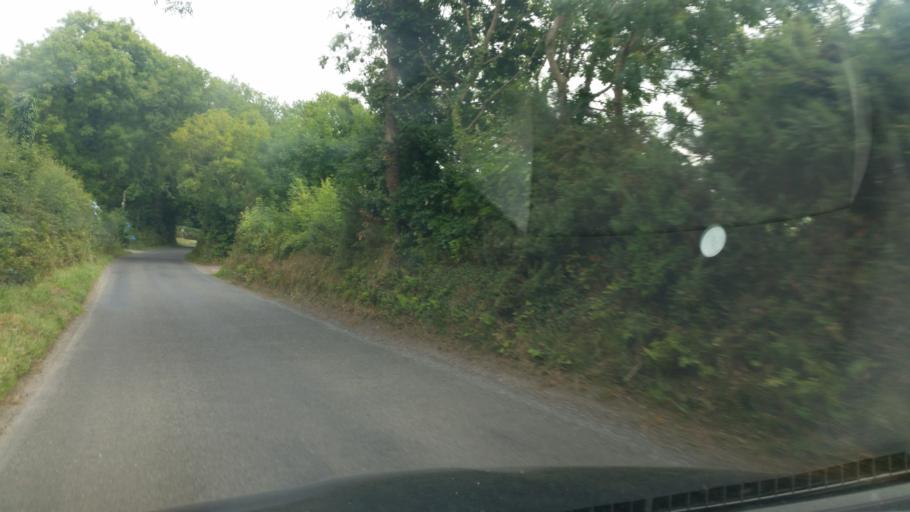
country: IE
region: Leinster
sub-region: Loch Garman
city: Bunclody
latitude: 52.6487
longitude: -6.7294
